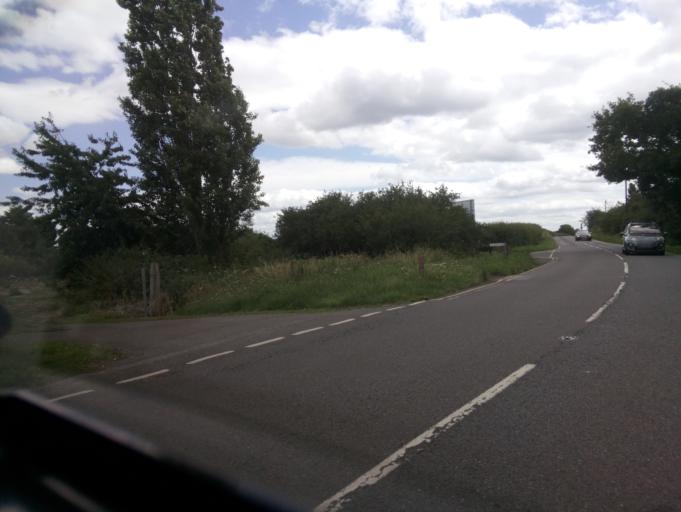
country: GB
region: England
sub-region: Nottinghamshire
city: West Bridgford
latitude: 52.9219
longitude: -1.0911
